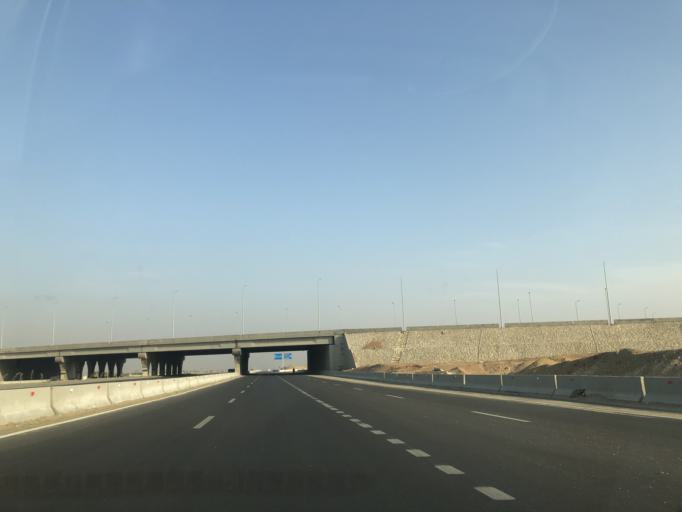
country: EG
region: Al Jizah
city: Madinat Sittah Uktubar
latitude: 29.8942
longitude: 31.0020
